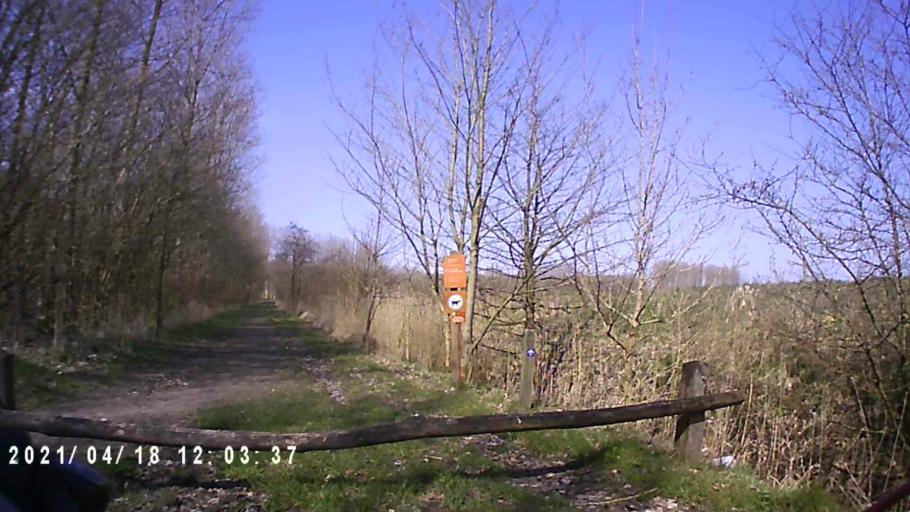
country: NL
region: Friesland
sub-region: Gemeente Kollumerland en Nieuwkruisland
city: Kollum
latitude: 53.3293
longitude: 6.1863
